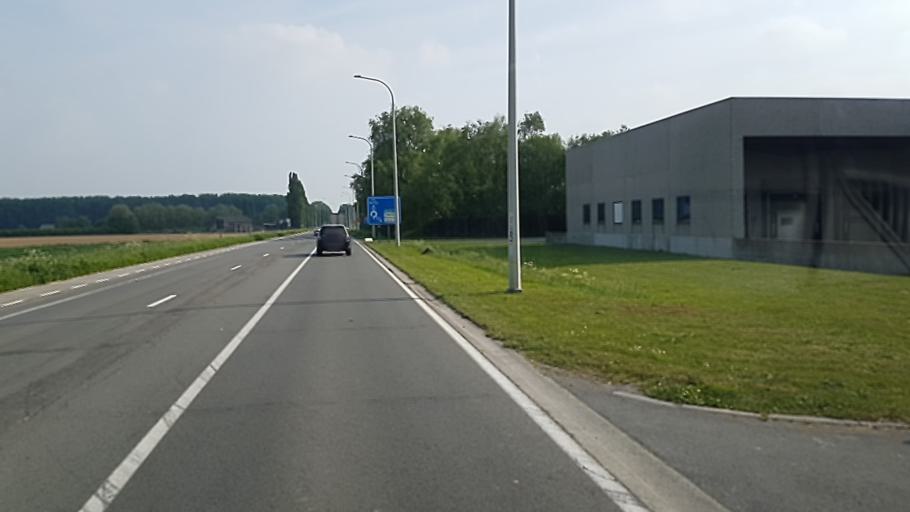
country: BE
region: Wallonia
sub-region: Province du Hainaut
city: Pecq
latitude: 50.7218
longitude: 3.3317
